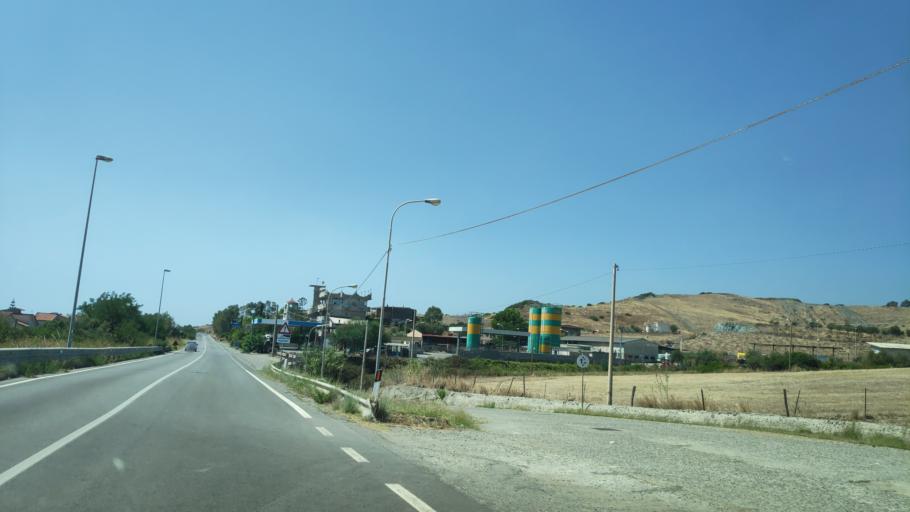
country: IT
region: Calabria
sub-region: Provincia di Reggio Calabria
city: Africo Nuovo
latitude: 38.0105
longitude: 16.1304
